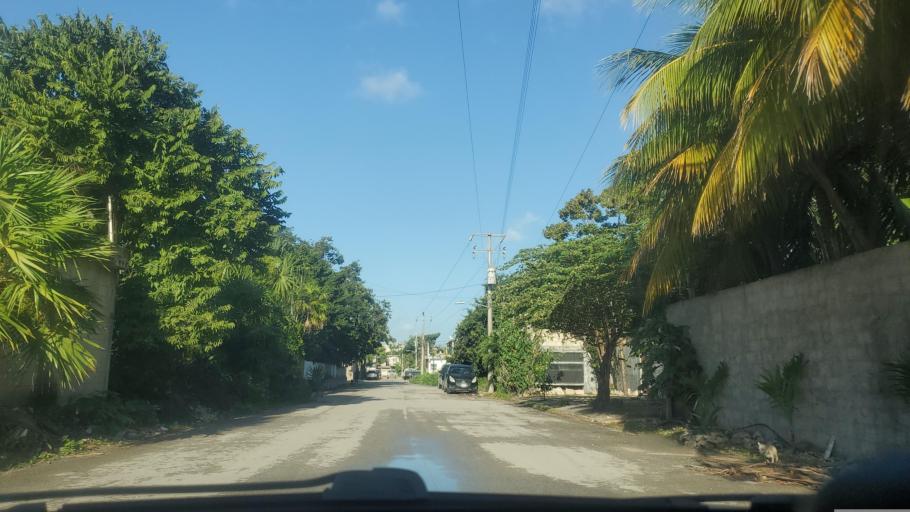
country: MX
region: Quintana Roo
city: Tulum
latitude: 20.2129
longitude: -87.4687
